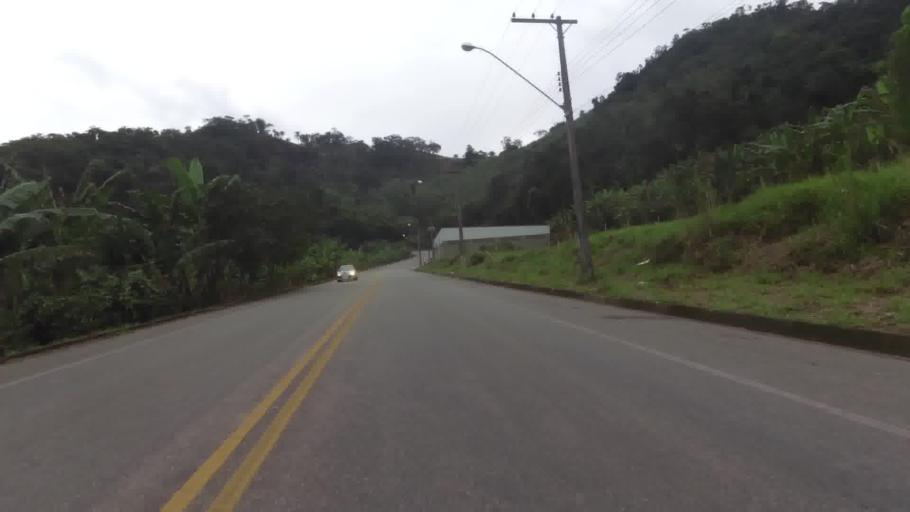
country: BR
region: Espirito Santo
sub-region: Iconha
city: Iconha
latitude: -20.7851
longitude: -40.8112
